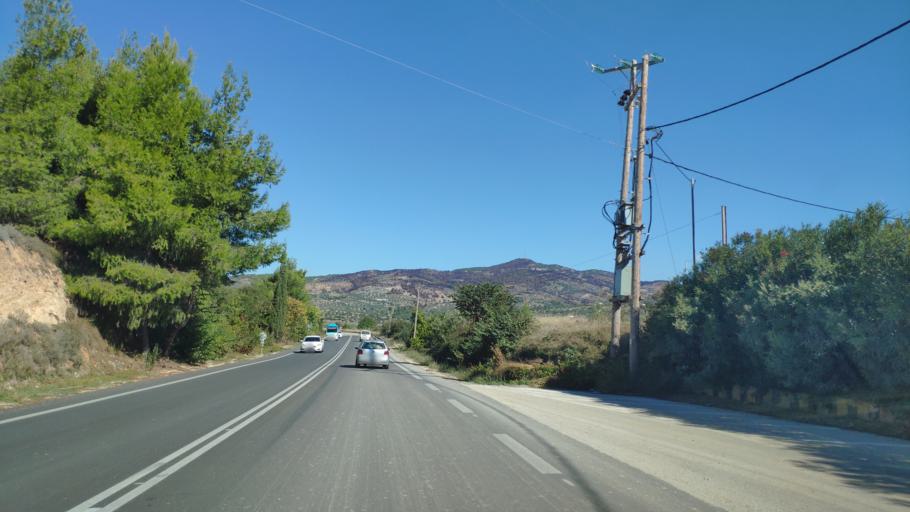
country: GR
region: Peloponnese
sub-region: Nomos Korinthias
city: Athikia
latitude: 37.8369
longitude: 22.8984
